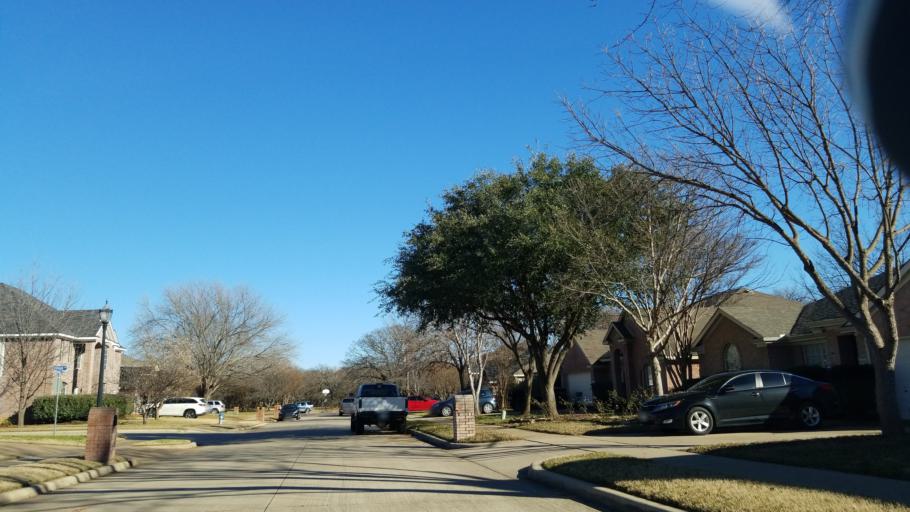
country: US
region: Texas
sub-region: Denton County
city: Corinth
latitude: 33.1375
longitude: -97.0834
